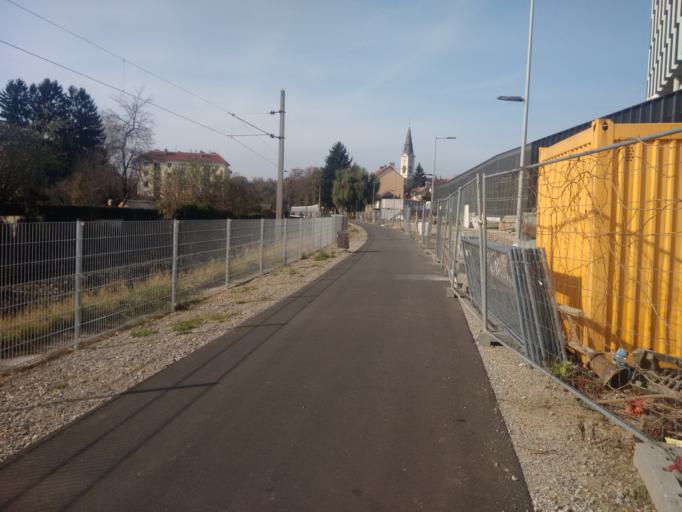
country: AT
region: Styria
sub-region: Graz Stadt
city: Graz
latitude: 47.0565
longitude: 15.4458
